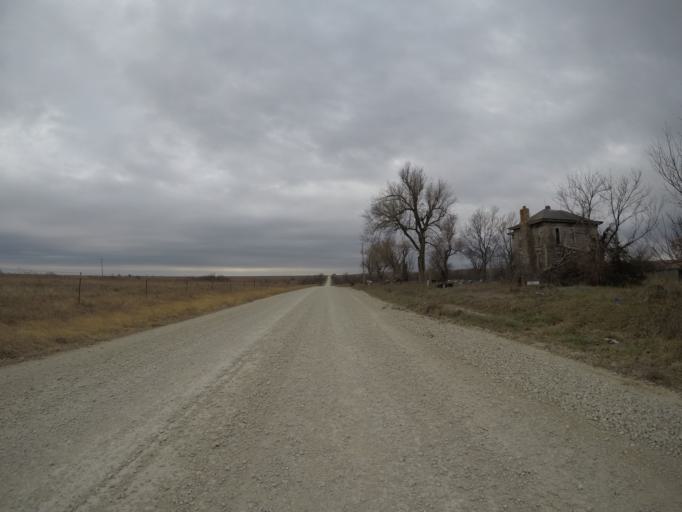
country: US
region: Kansas
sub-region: Wabaunsee County
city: Alma
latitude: 38.7745
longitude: -96.1498
